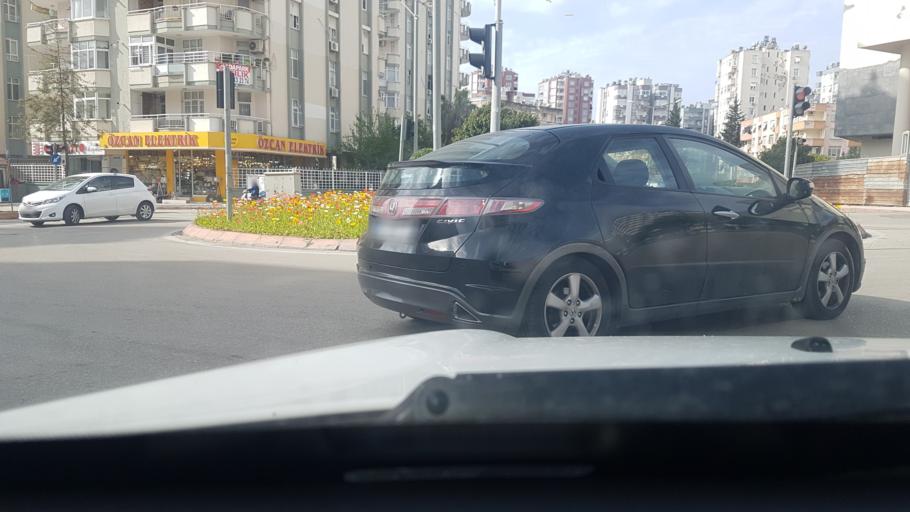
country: TR
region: Adana
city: Adana
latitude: 37.0430
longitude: 35.3024
